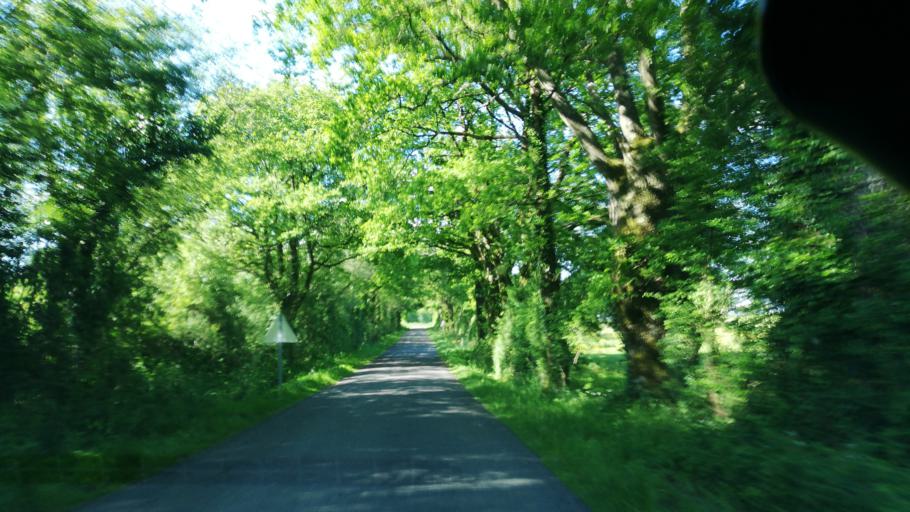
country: FR
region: Poitou-Charentes
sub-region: Departement des Deux-Sevres
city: Moncoutant
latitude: 46.6716
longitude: -0.5703
